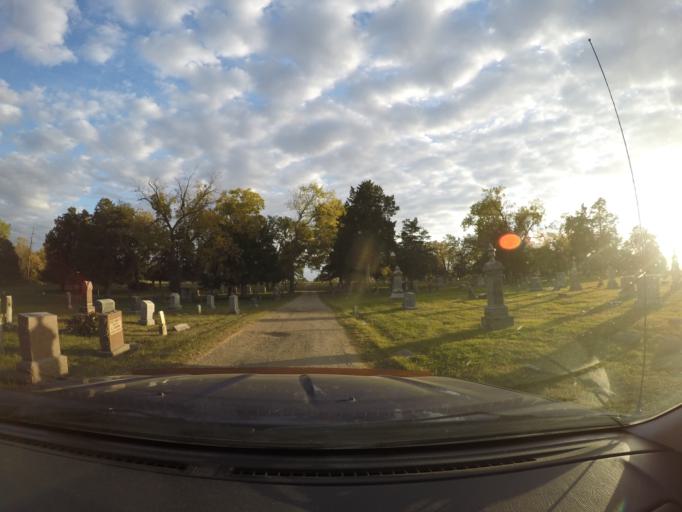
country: US
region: Kansas
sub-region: Shawnee County
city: Topeka
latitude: 39.0420
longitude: -95.6519
